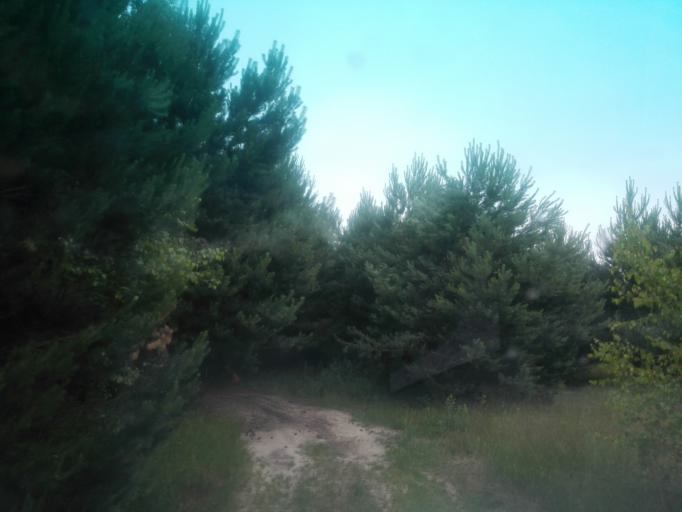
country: PL
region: Silesian Voivodeship
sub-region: Powiat czestochowski
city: Olsztyn
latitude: 50.7881
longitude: 19.2703
